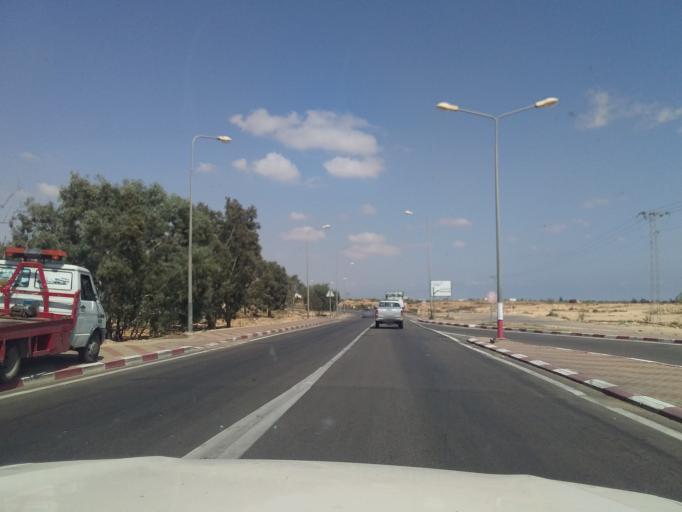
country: TN
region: Madanin
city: Medenine
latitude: 33.5914
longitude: 10.3140
